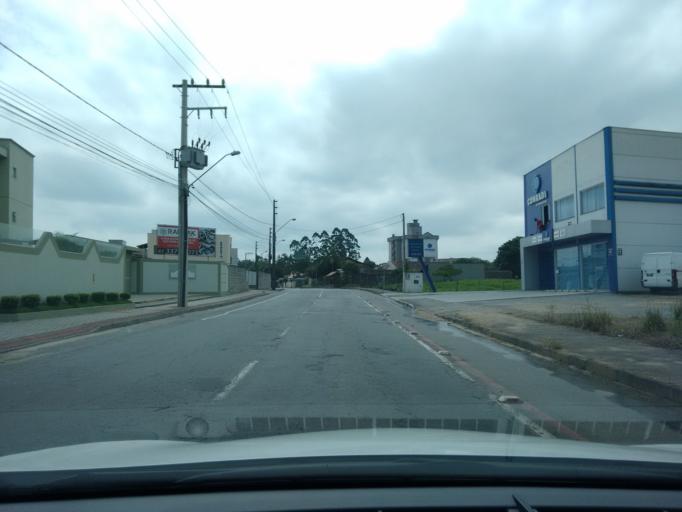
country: BR
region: Santa Catarina
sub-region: Jaragua Do Sul
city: Jaragua do Sul
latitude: -26.4892
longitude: -49.0631
